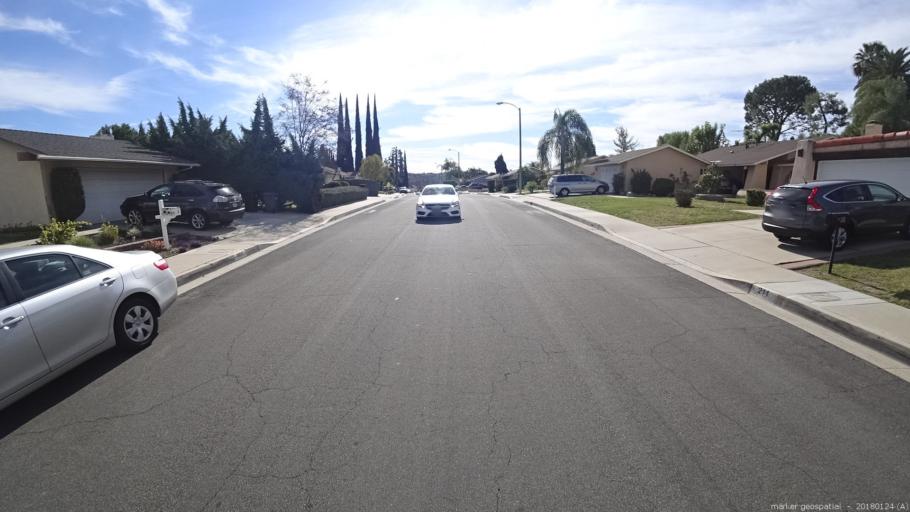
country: US
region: California
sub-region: Los Angeles County
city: Diamond Bar
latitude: 34.0248
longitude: -117.8137
